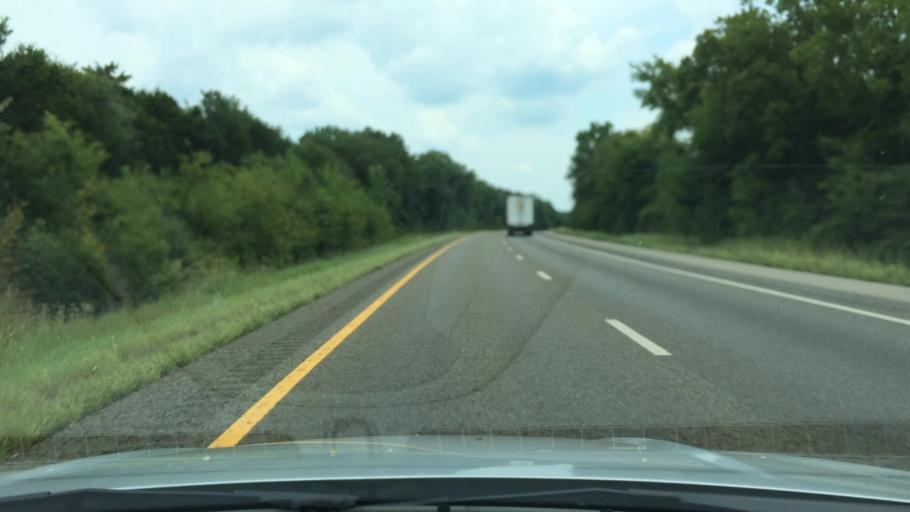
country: US
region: Tennessee
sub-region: Maury County
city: Columbia
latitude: 35.5495
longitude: -86.9076
